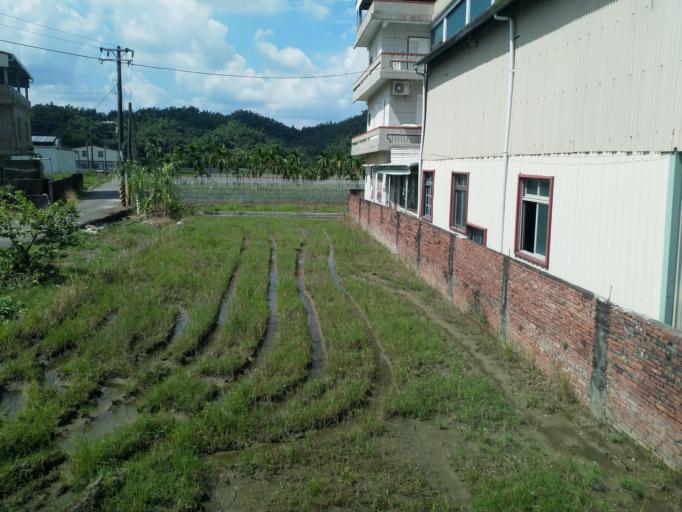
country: TW
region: Taiwan
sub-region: Pingtung
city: Pingtung
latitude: 22.8841
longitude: 120.5773
